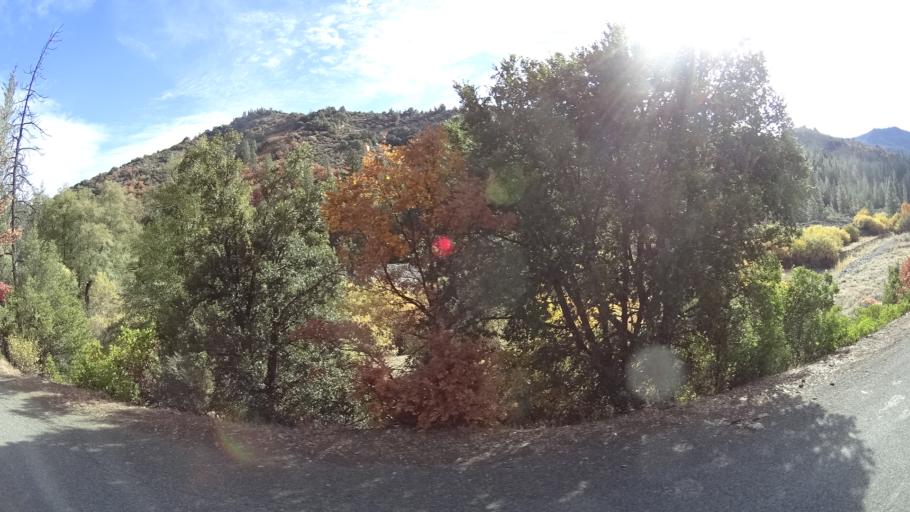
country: US
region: California
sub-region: Siskiyou County
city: Yreka
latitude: 41.7025
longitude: -122.8172
